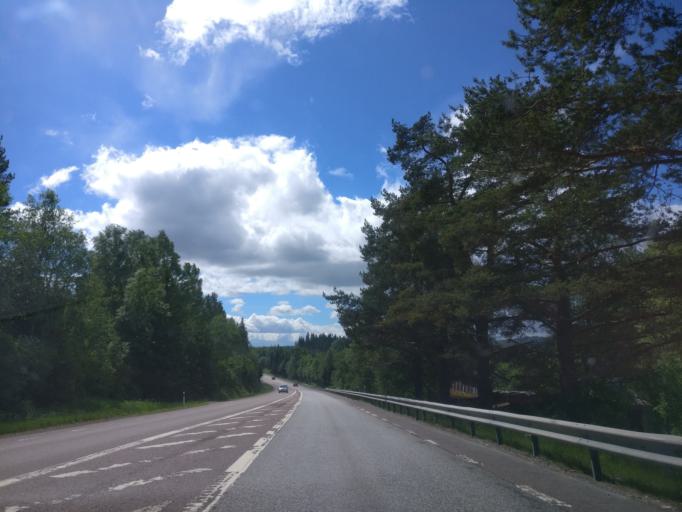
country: SE
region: Vaesternorrland
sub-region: Haernoesands Kommun
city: Haernoesand
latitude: 62.7057
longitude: 17.8648
